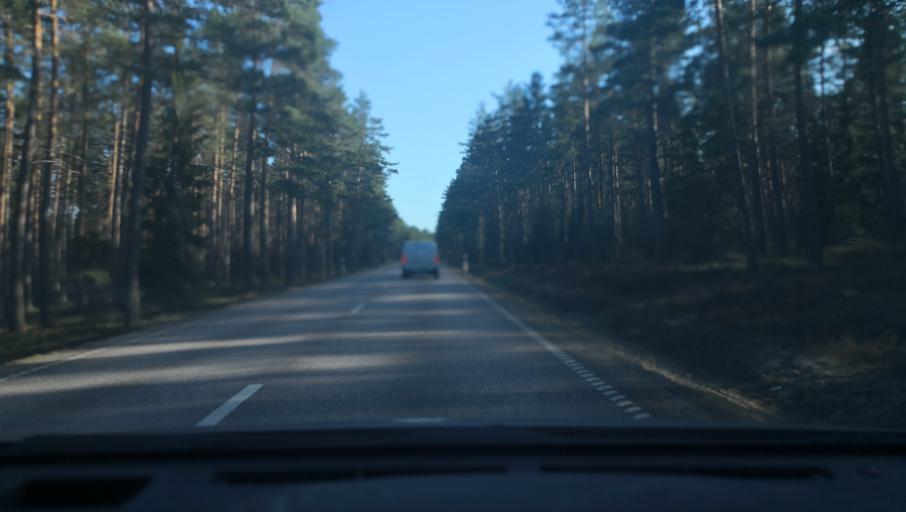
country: SE
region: Uppsala
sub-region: Heby Kommun
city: Tarnsjo
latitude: 60.1130
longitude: 16.8856
